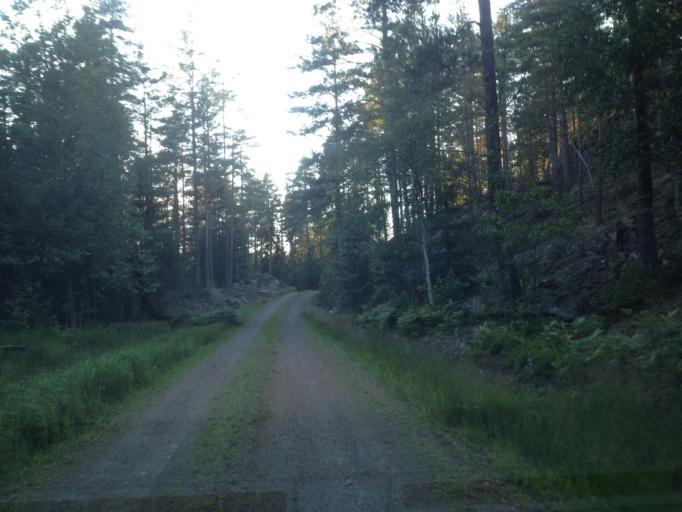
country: SE
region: Kalmar
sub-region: Vasterviks Kommun
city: Overum
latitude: 58.0002
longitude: 16.1543
